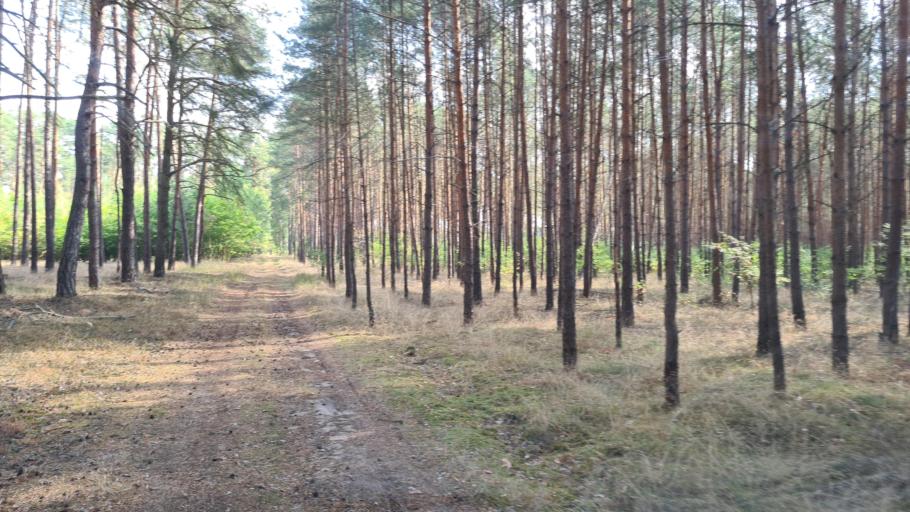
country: DE
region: Brandenburg
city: Belzig
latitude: 52.1630
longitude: 12.6544
